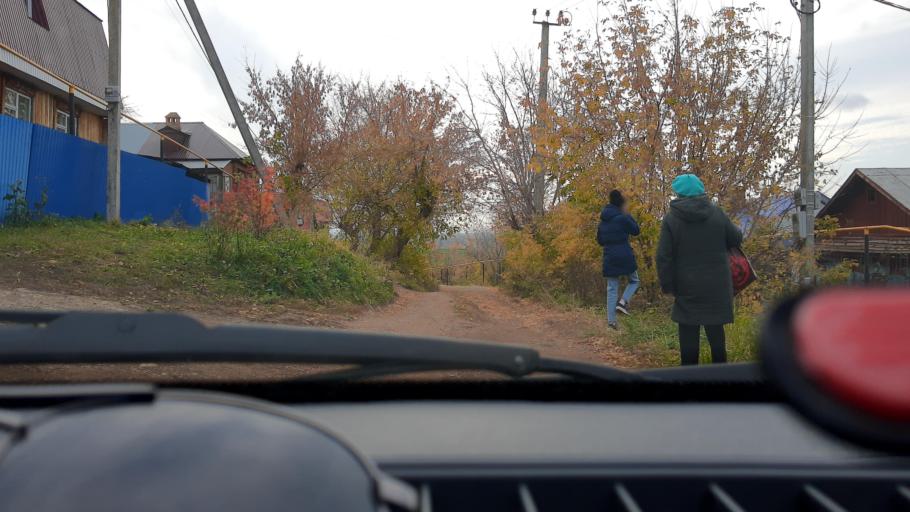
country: RU
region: Bashkortostan
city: Ufa
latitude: 54.7025
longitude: 55.9736
